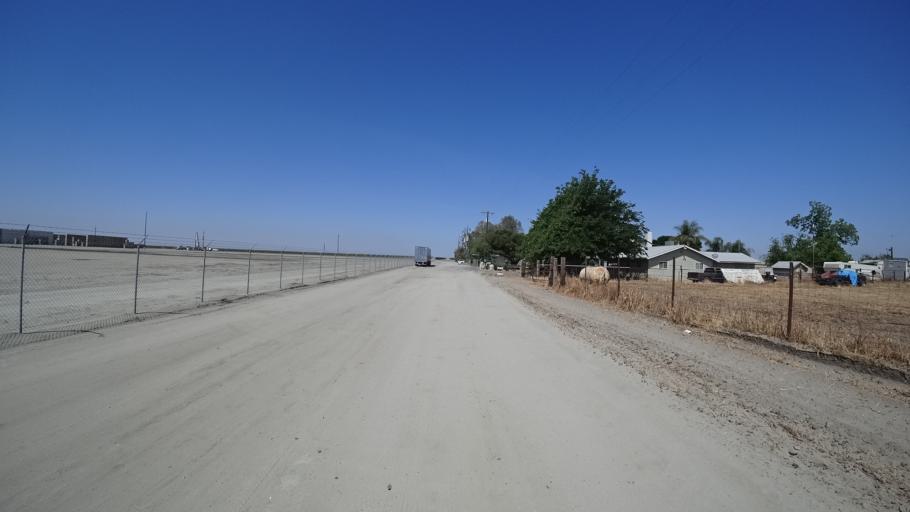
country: US
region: California
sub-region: Kings County
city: Corcoran
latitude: 36.0725
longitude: -119.5694
